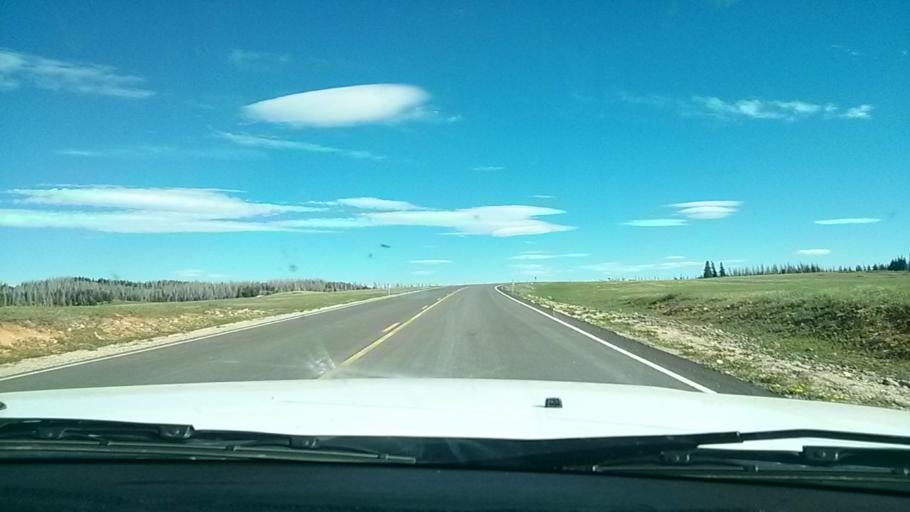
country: US
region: Utah
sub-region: Iron County
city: Parowan
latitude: 37.6686
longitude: -112.8393
